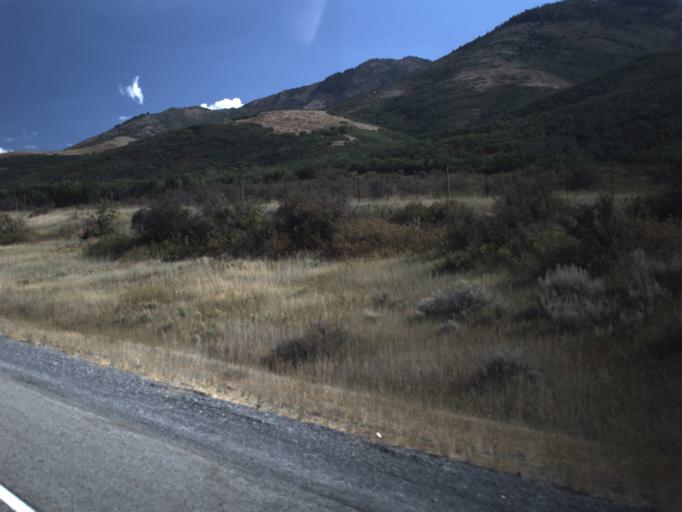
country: US
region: Utah
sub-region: Summit County
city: Summit Park
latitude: 40.7492
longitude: -111.7105
